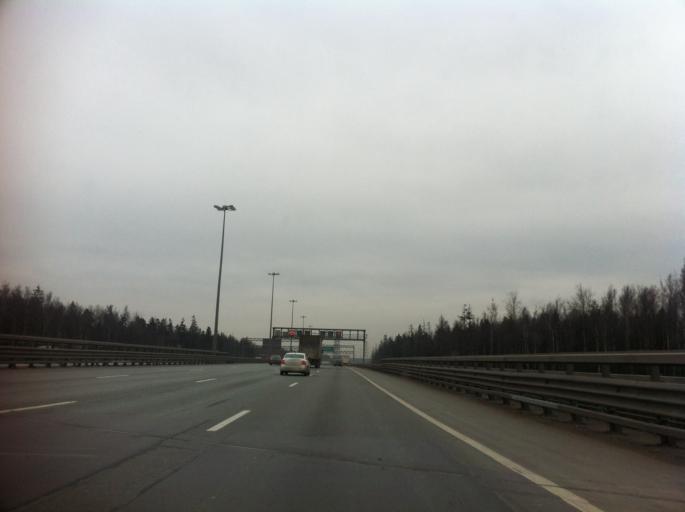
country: RU
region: St.-Petersburg
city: Krasnogvargeisky
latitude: 59.9410
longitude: 30.5390
